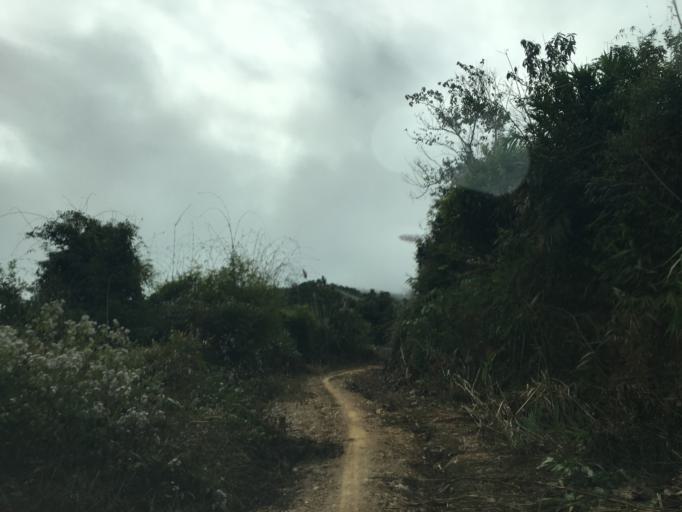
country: LA
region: Houaphan
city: Viengthong
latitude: 19.9395
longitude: 103.2994
